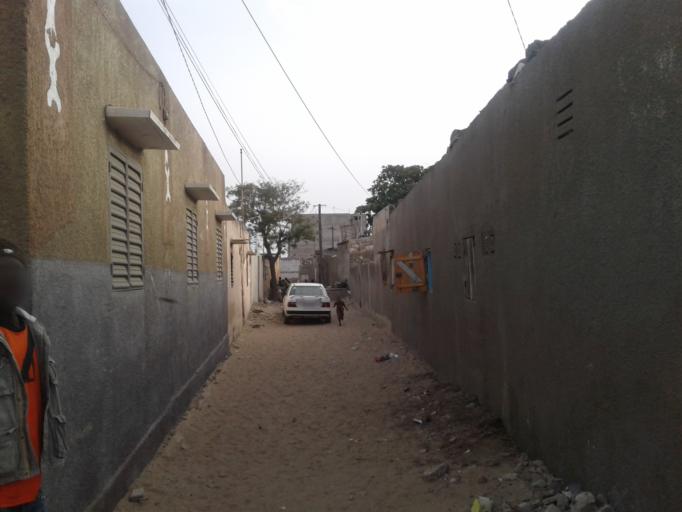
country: SN
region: Dakar
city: Pikine
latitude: 14.7692
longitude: -17.3836
